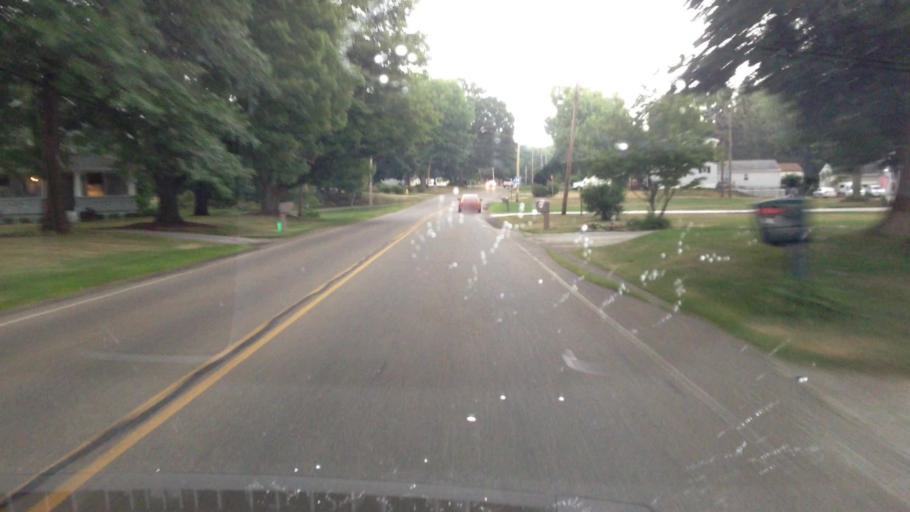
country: US
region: Ohio
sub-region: Summit County
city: Barberton
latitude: 41.0169
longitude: -81.5775
